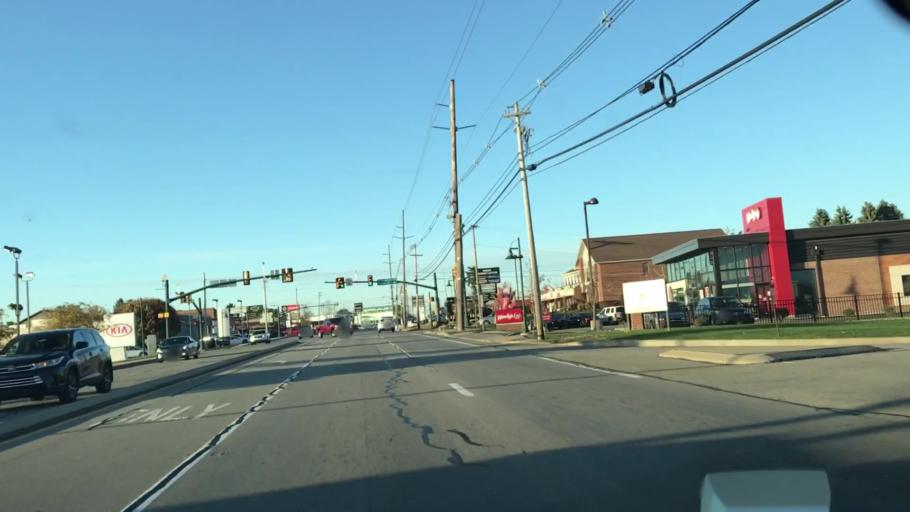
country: US
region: Pennsylvania
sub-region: Allegheny County
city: Bradford Woods
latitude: 40.6152
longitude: -80.0551
